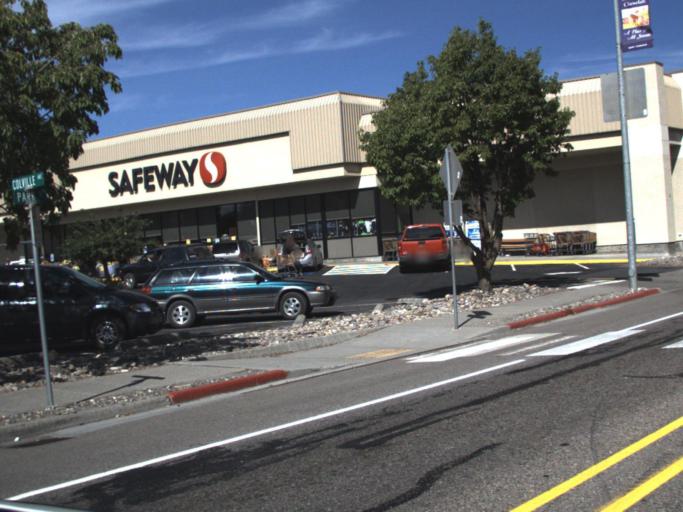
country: US
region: Washington
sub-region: Stevens County
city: Chewelah
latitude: 48.2790
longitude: -117.7154
